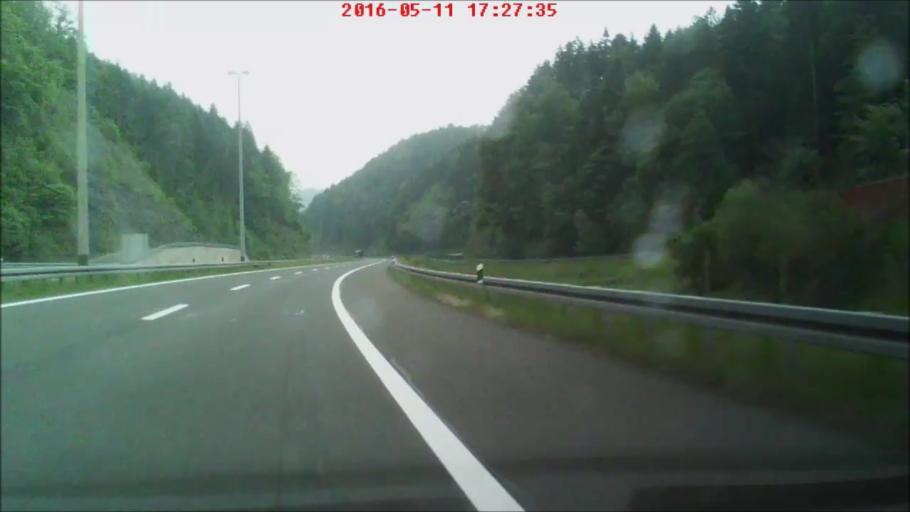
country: SI
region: Zetale
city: Zetale
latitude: 46.2384
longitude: 15.8470
